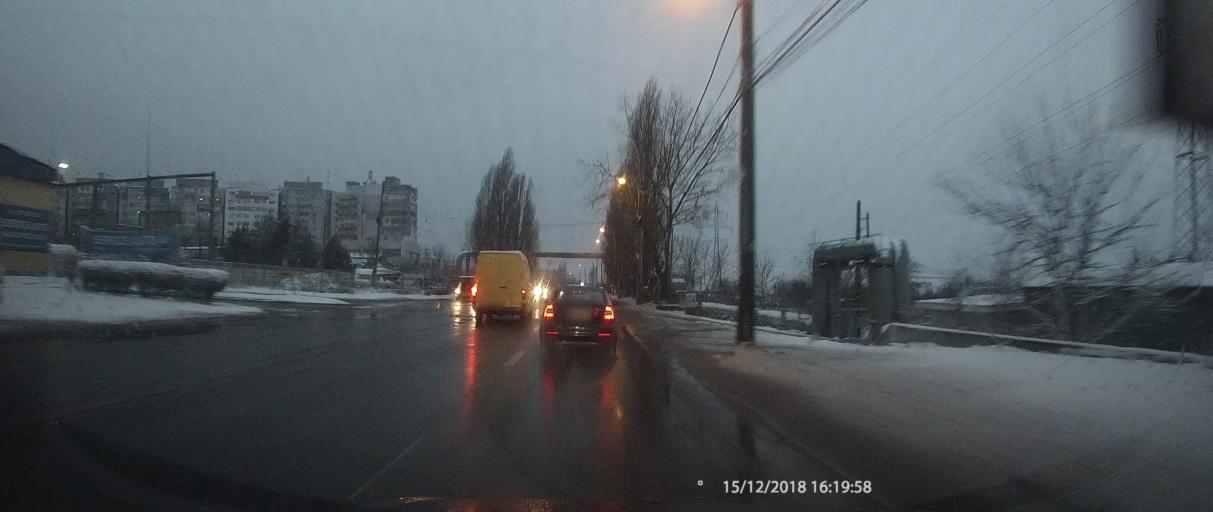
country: RO
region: Galati
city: Galati
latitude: 45.4164
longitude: 28.0049
